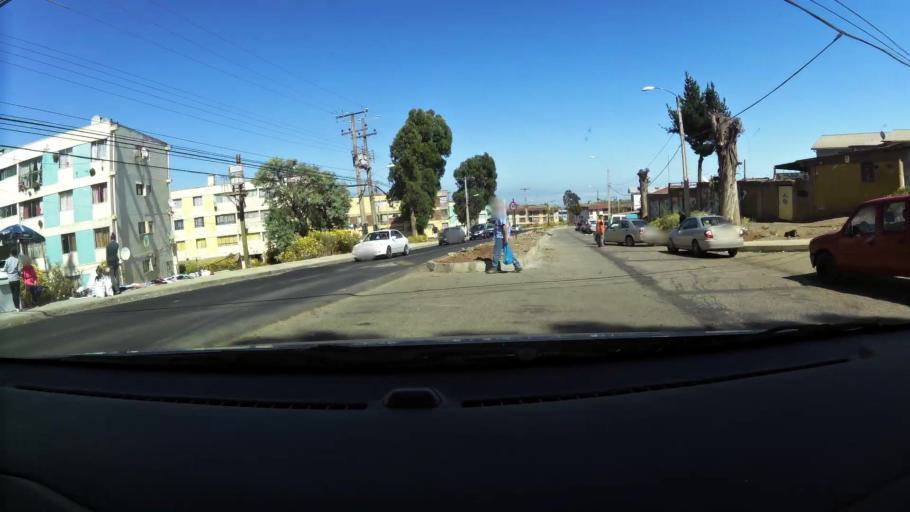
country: CL
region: Valparaiso
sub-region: Provincia de Valparaiso
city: Valparaiso
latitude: -33.0501
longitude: -71.6500
